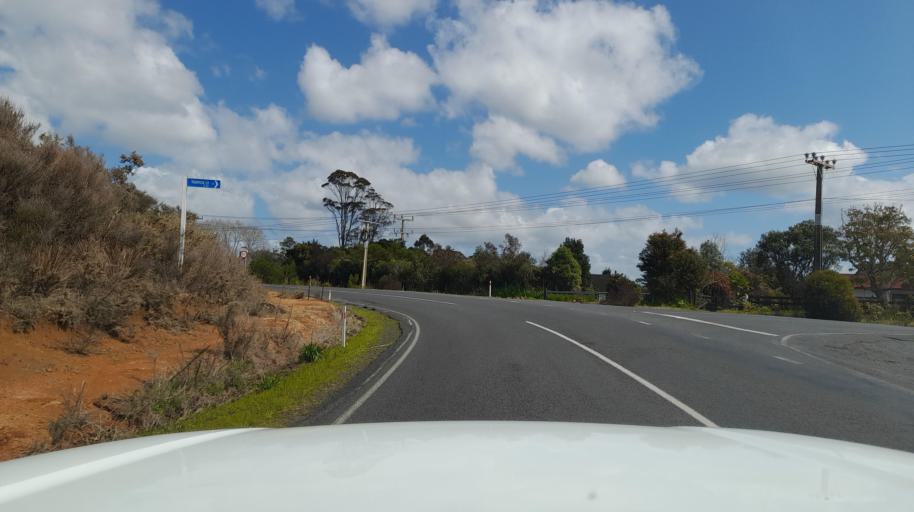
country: NZ
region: Northland
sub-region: Far North District
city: Kerikeri
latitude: -35.2497
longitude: 173.9095
